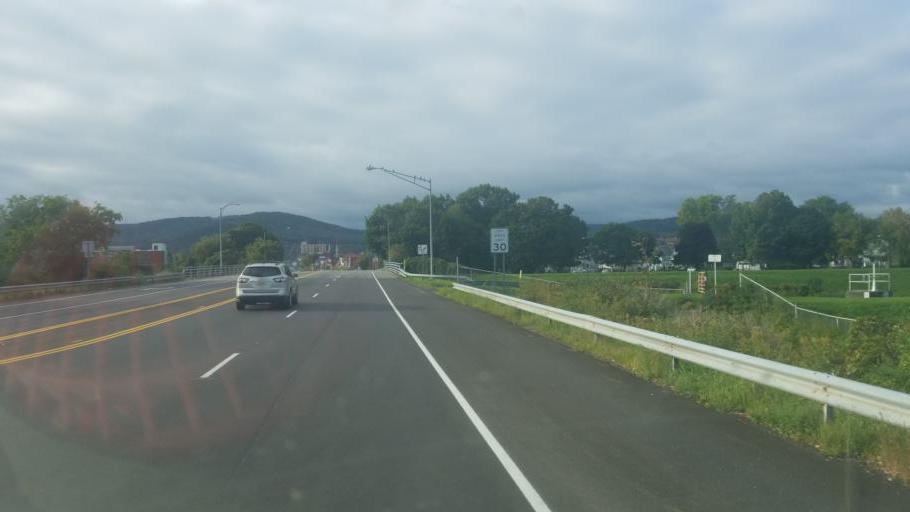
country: US
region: New York
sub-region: Cattaraugus County
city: Olean
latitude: 42.0895
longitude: -78.4298
